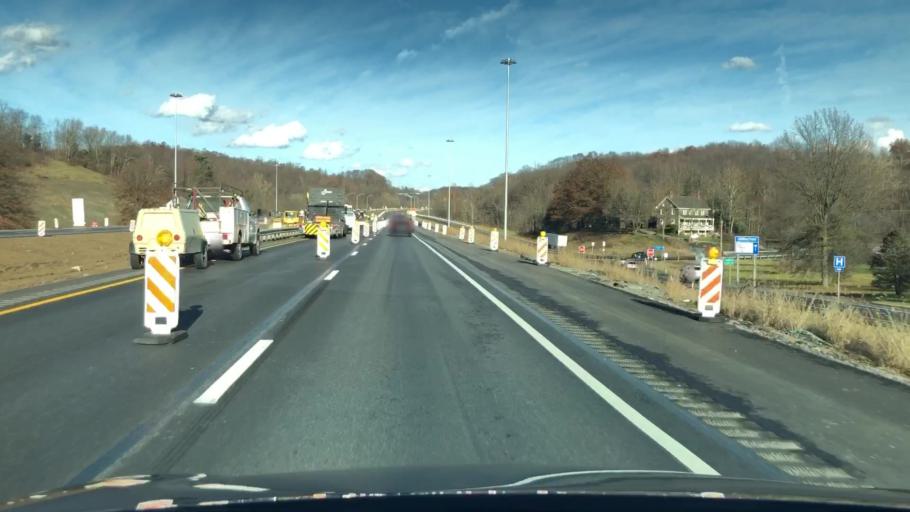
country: US
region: Pennsylvania
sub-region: Allegheny County
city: Brackenridge
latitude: 40.6305
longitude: -79.7333
